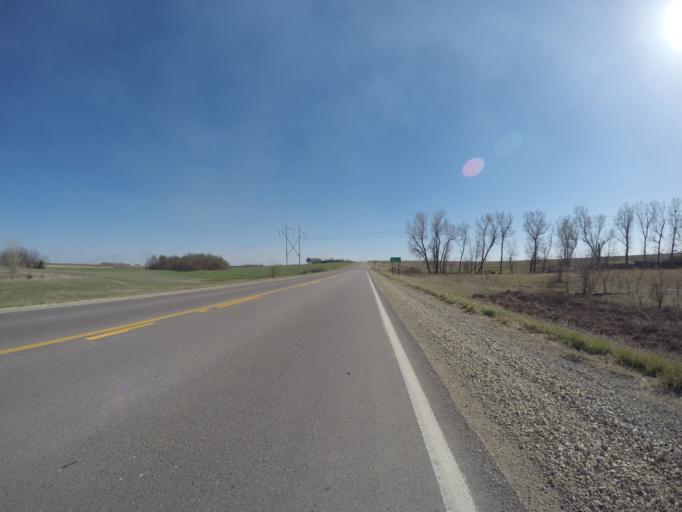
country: US
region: Kansas
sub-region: Riley County
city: Fort Riley North
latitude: 39.2976
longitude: -96.7749
